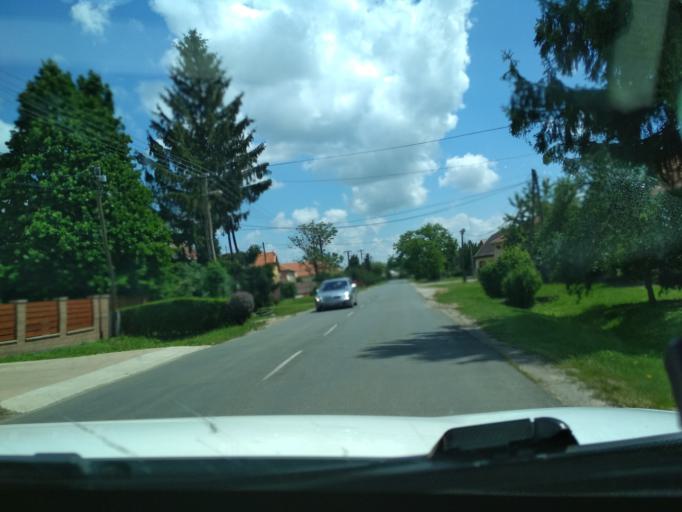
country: HU
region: Jasz-Nagykun-Szolnok
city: Tiszafured
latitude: 47.6132
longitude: 20.7739
